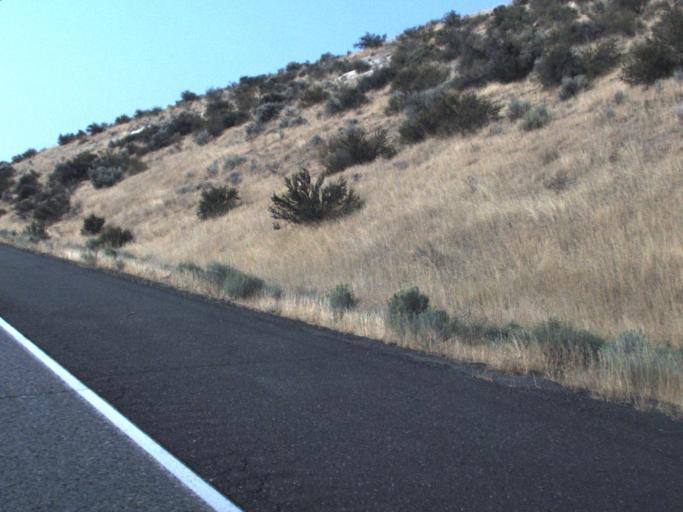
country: US
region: Washington
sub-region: Yakima County
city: Terrace Heights
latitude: 46.7806
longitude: -120.3737
